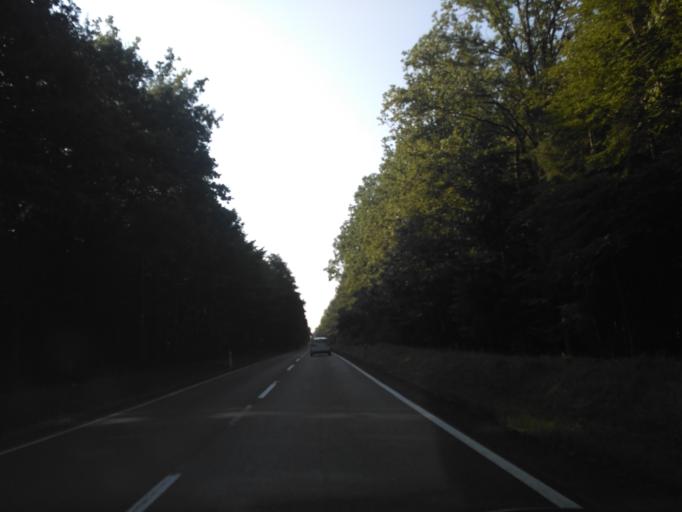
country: PL
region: Subcarpathian Voivodeship
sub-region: Powiat nizanski
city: Raclawice
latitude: 50.4829
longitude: 22.1448
